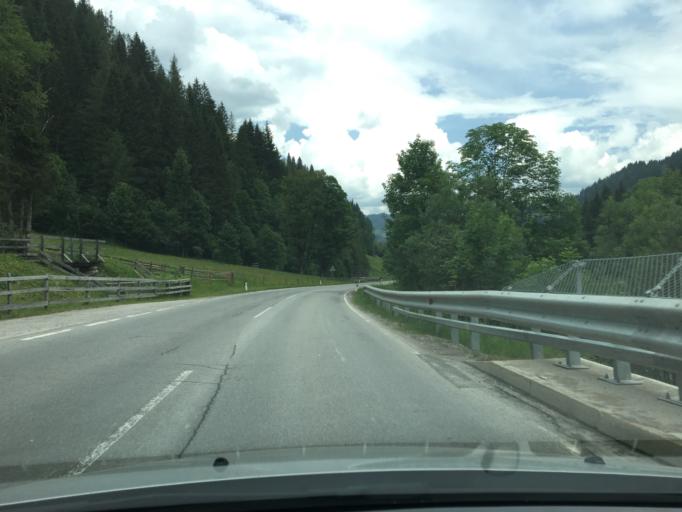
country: AT
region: Salzburg
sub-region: Politischer Bezirk Sankt Johann im Pongau
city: Wagrain
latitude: 47.3120
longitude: 13.3031
